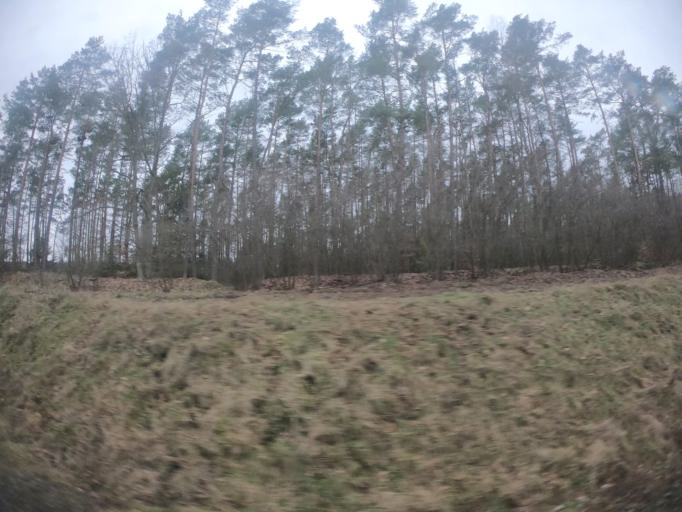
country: PL
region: West Pomeranian Voivodeship
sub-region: Powiat szczecinecki
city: Bialy Bor
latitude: 53.8284
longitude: 16.8726
